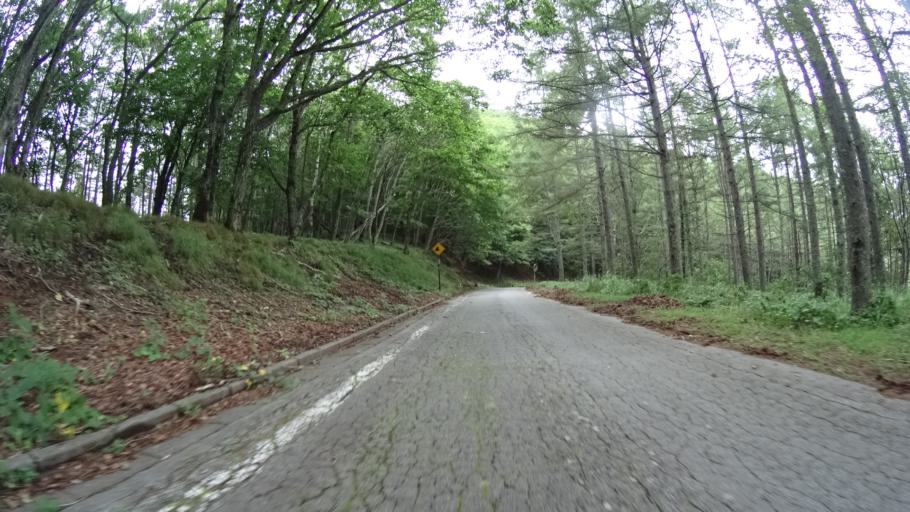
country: JP
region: Yamanashi
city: Kofu-shi
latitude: 35.8217
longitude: 138.5550
